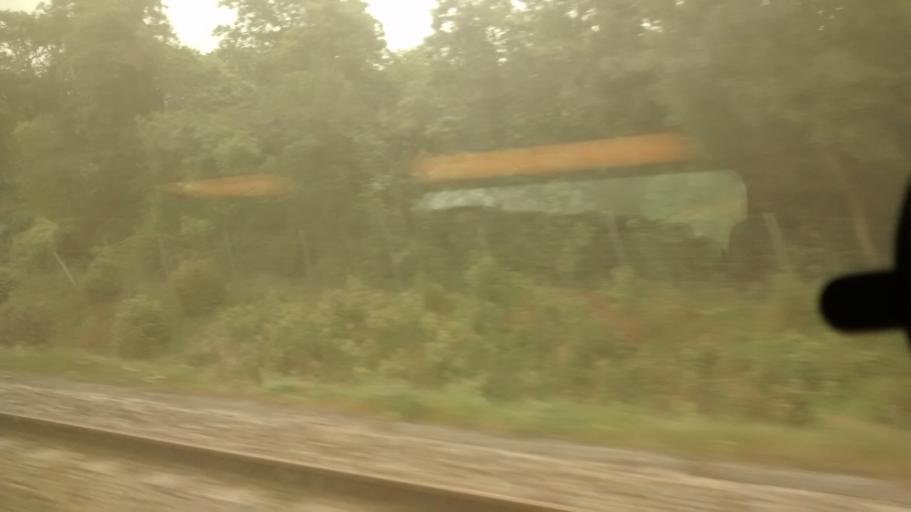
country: FR
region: Ile-de-France
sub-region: Departement de l'Essonne
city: Angervilliers
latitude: 48.5964
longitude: 2.0532
